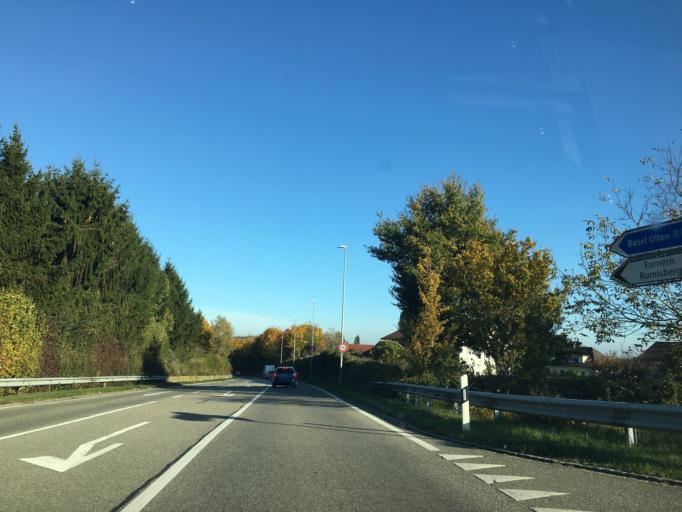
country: CH
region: Bern
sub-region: Oberaargau
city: Wiedlisbach
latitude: 47.2488
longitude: 7.6385
